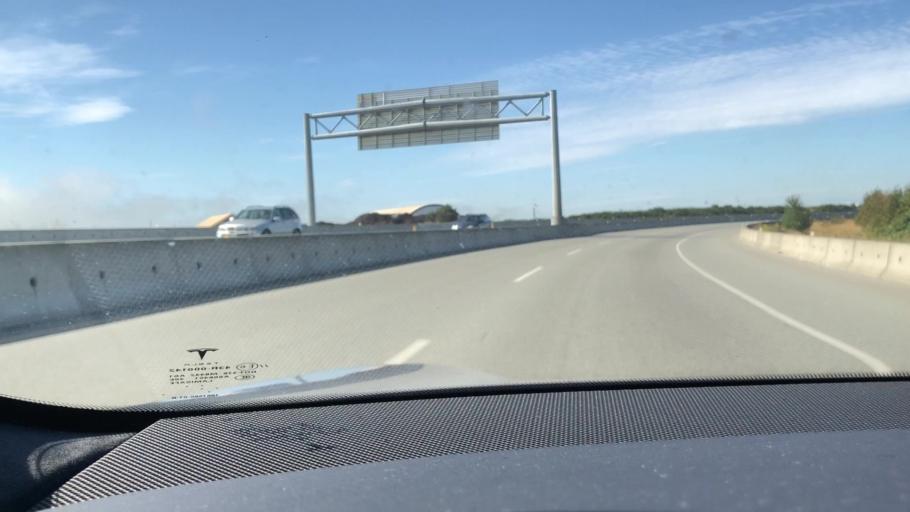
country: CA
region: British Columbia
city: Ladner
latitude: 49.0843
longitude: -123.0256
